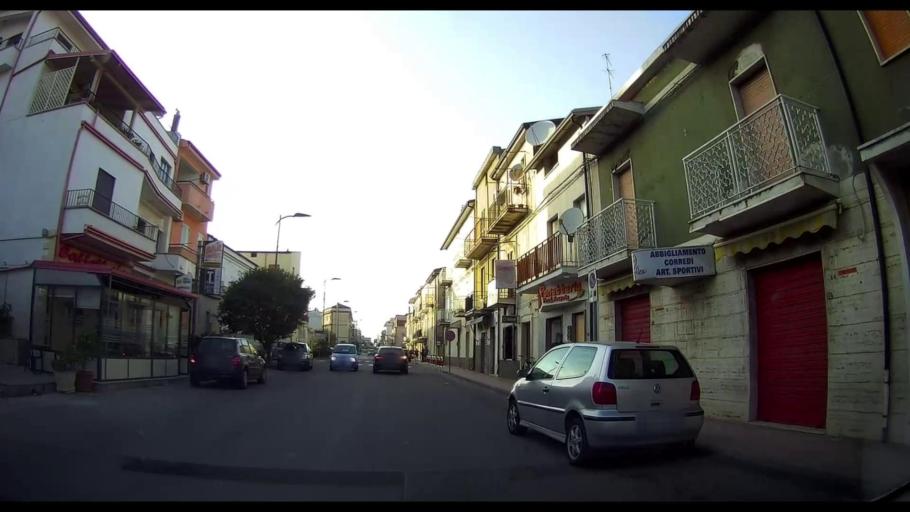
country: IT
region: Calabria
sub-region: Provincia di Crotone
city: Torretta
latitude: 39.4506
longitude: 17.0391
